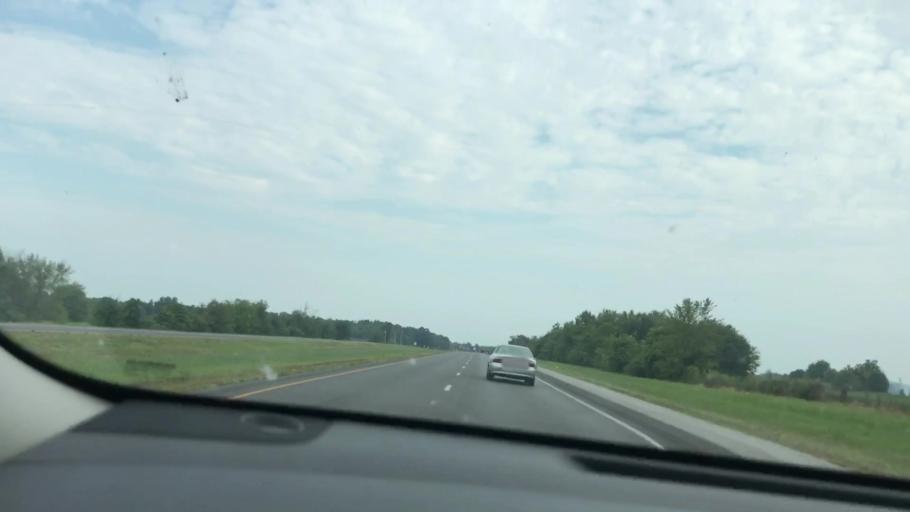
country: US
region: Kentucky
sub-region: Calloway County
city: Murray
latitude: 36.6929
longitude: -88.3030
